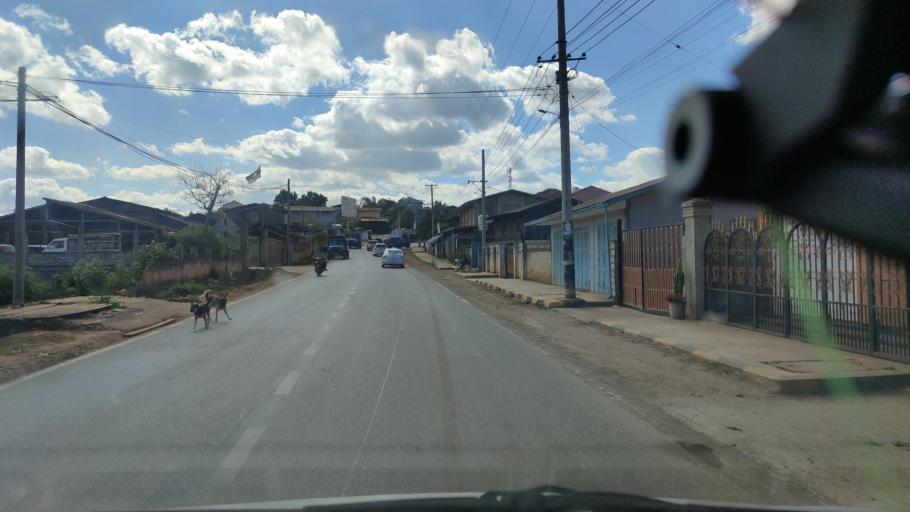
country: MM
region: Shan
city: Taunggyi
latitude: 20.9980
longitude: 97.5354
